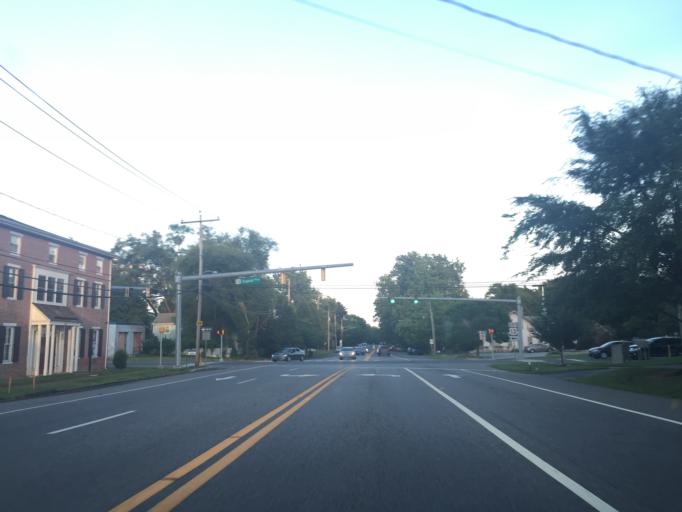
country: US
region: Delaware
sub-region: New Castle County
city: Middletown
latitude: 39.4568
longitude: -75.6612
